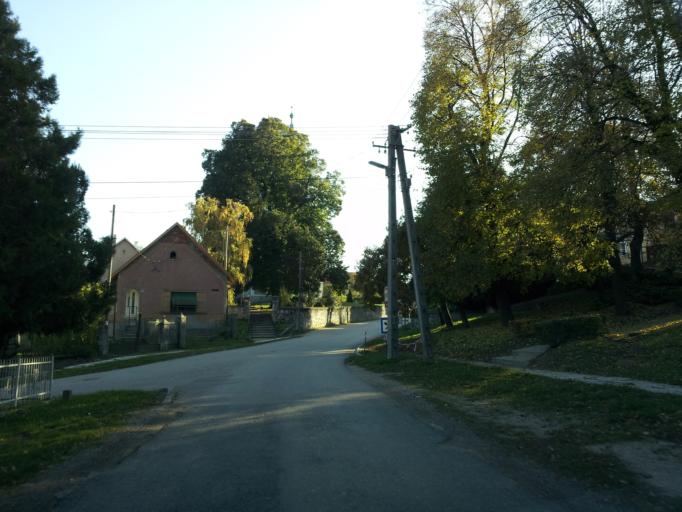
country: HU
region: Fejer
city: Fehervarcsurgo
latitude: 47.2899
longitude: 18.2630
